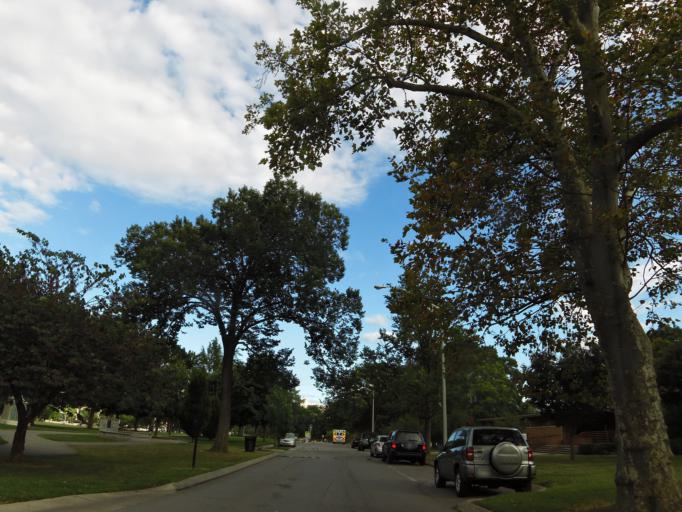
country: US
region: Tennessee
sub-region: Davidson County
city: Nashville
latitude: 36.1481
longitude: -86.8132
